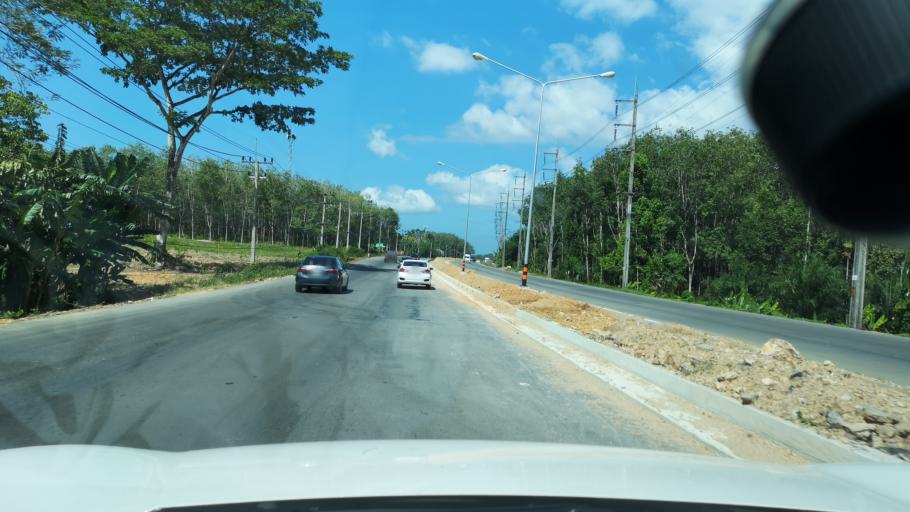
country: TH
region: Phangnga
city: Thai Mueang
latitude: 8.4351
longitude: 98.2573
